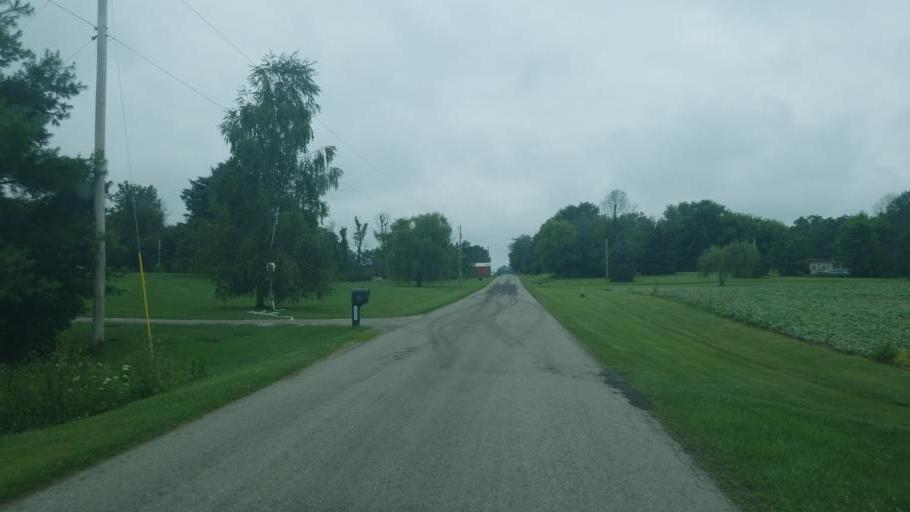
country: US
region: Ohio
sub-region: Knox County
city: Centerburg
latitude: 40.4094
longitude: -82.7492
